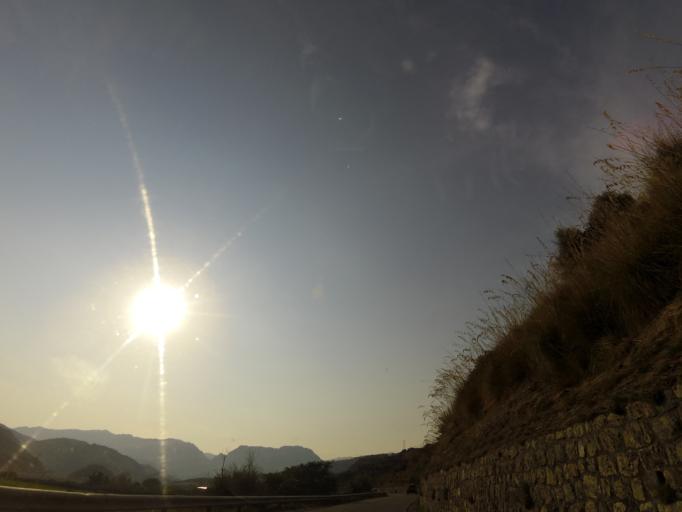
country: IT
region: Calabria
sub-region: Provincia di Reggio Calabria
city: Monasterace
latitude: 38.4629
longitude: 16.5162
